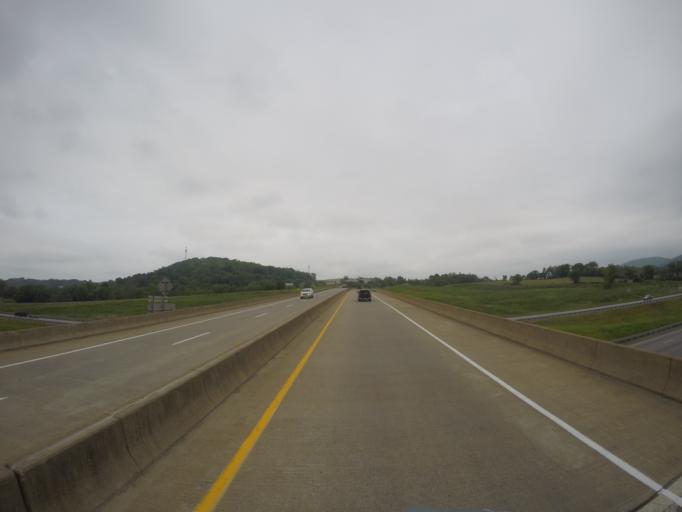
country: US
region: Virginia
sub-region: Augusta County
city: Jolivue
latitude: 38.1065
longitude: -79.0597
